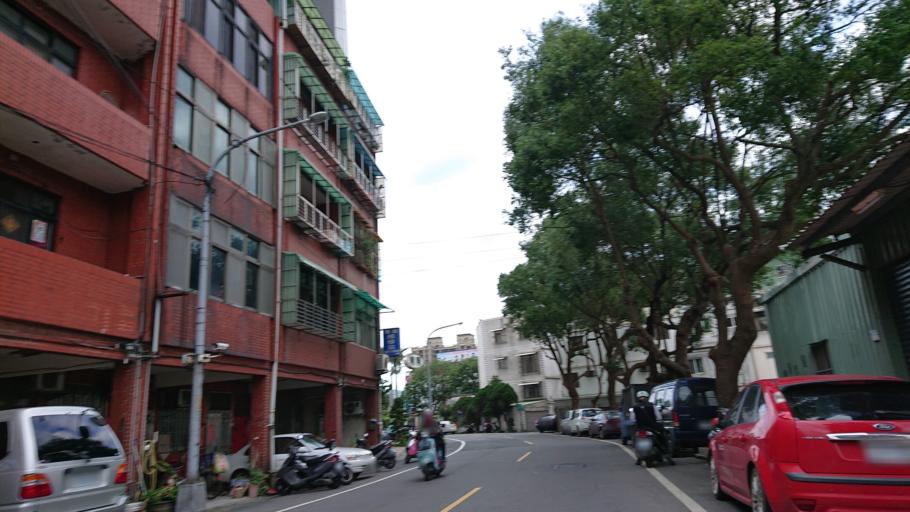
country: TW
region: Taiwan
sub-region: Taoyuan
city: Taoyuan
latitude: 24.9311
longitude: 121.3788
